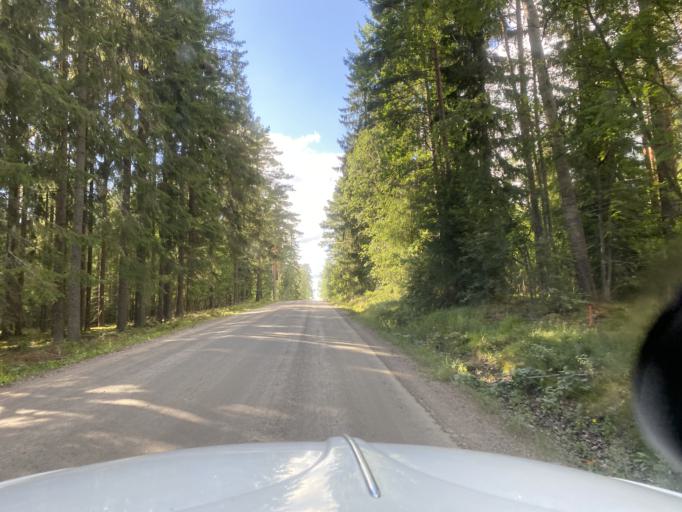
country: FI
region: Pirkanmaa
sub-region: Lounais-Pirkanmaa
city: Punkalaidun
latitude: 61.1394
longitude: 23.2134
